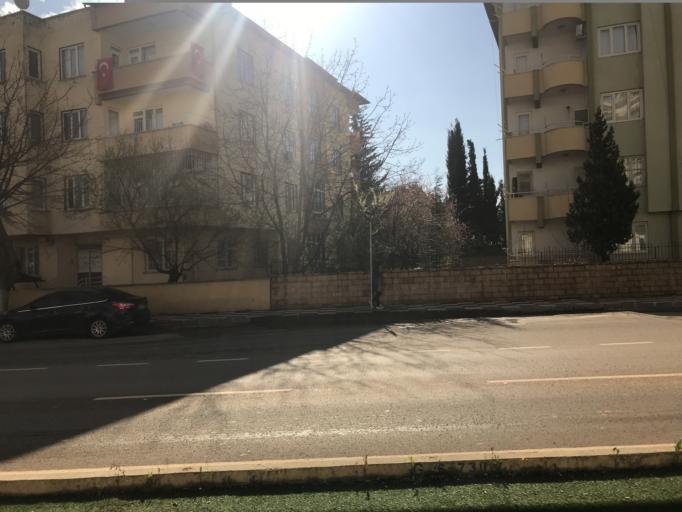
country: TR
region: Gaziantep
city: Sahinbey
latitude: 37.0551
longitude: 37.3301
